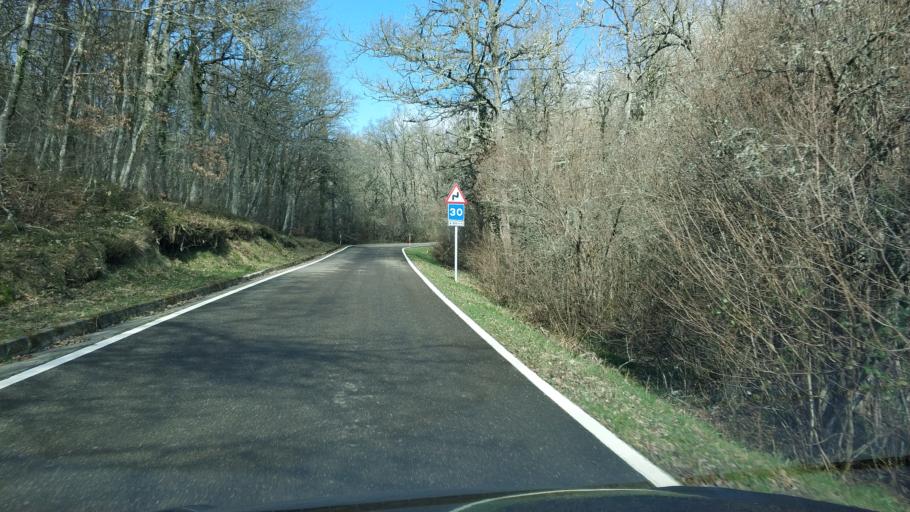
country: ES
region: Cantabria
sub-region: Provincia de Cantabria
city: Mataporquera
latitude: 42.9026
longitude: -4.0515
